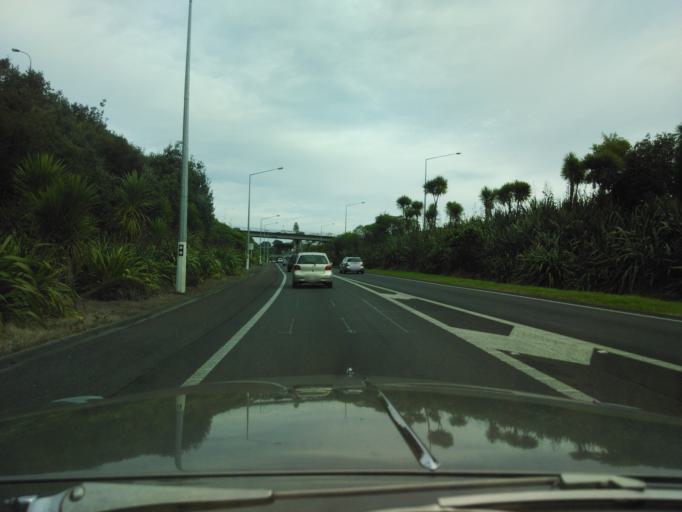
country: NZ
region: Auckland
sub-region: Auckland
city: Auckland
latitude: -36.8610
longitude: 174.7569
